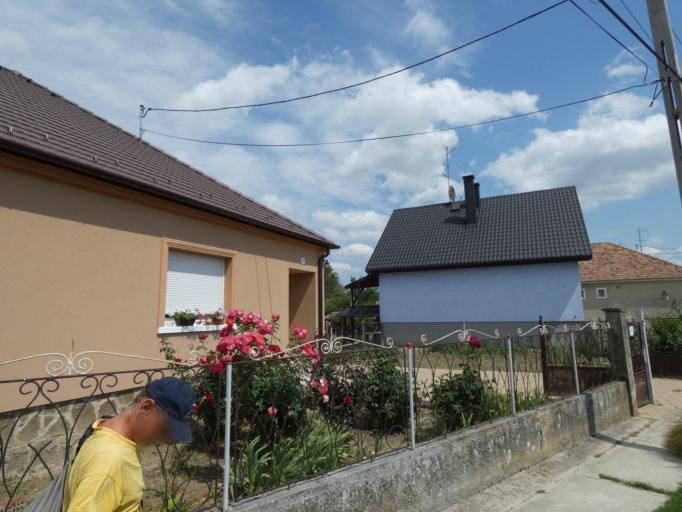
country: HU
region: Gyor-Moson-Sopron
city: Halaszi
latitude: 47.9538
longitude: 17.3447
